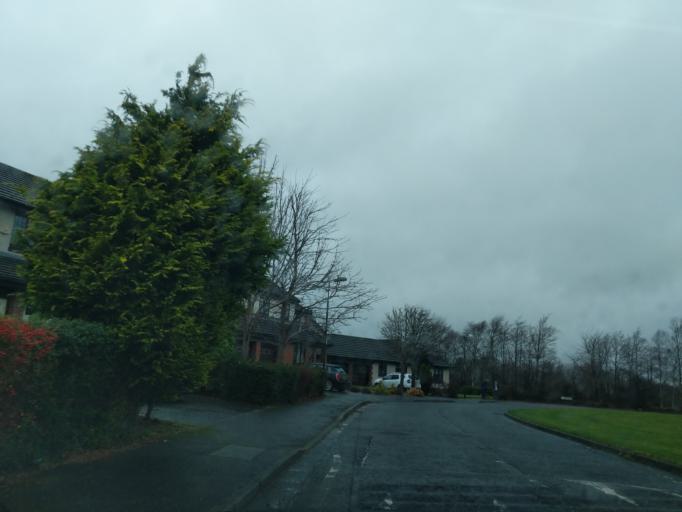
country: GB
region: Scotland
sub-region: Midlothian
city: Loanhead
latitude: 55.9057
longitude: -3.1746
